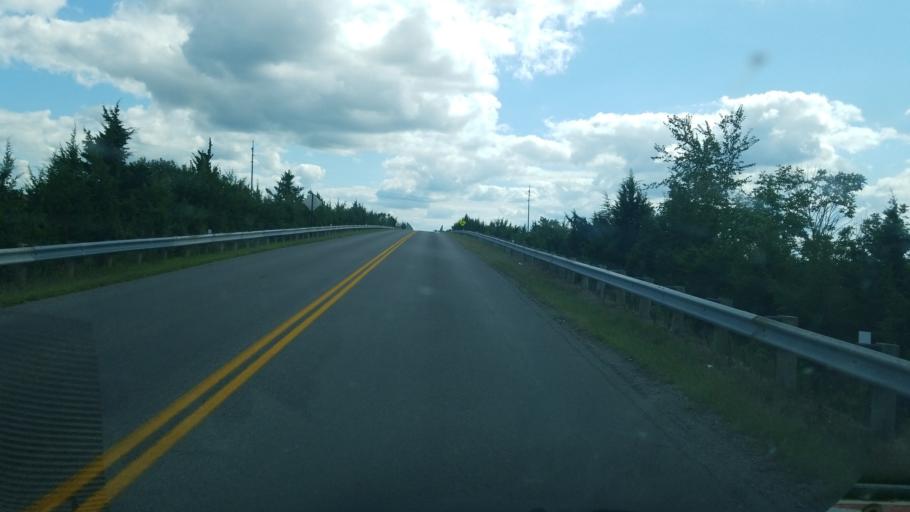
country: US
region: Ohio
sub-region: Allen County
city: Lima
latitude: 40.7735
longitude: -84.0706
